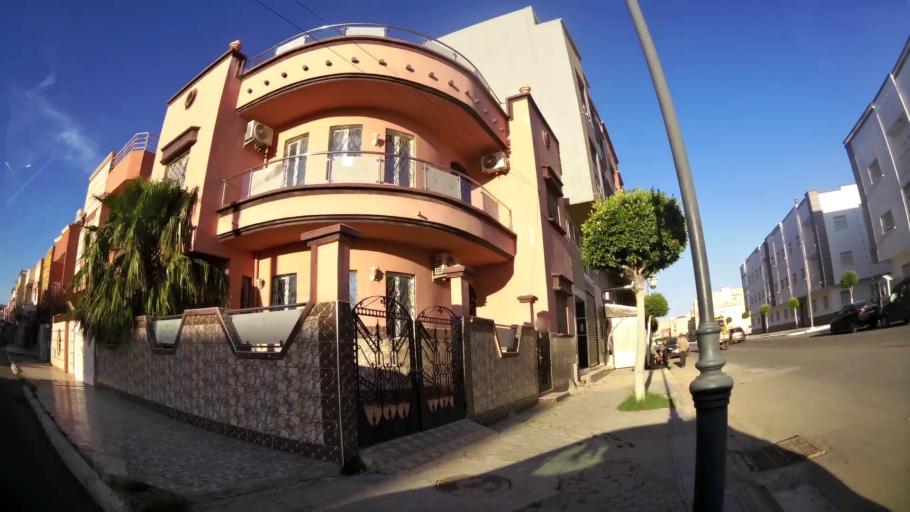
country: MA
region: Oriental
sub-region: Berkane-Taourirt
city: Madagh
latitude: 35.0811
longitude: -2.2388
